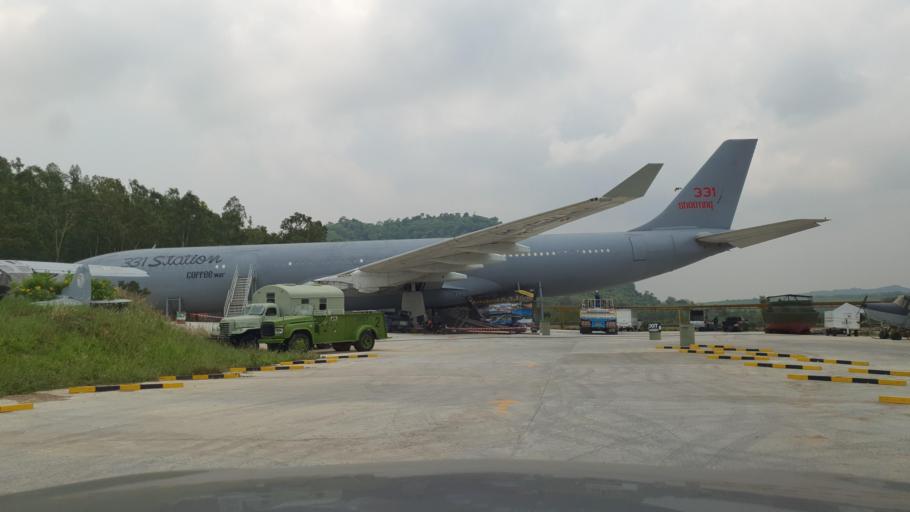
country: TH
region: Rayong
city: Ban Chang
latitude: 12.7574
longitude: 100.9905
